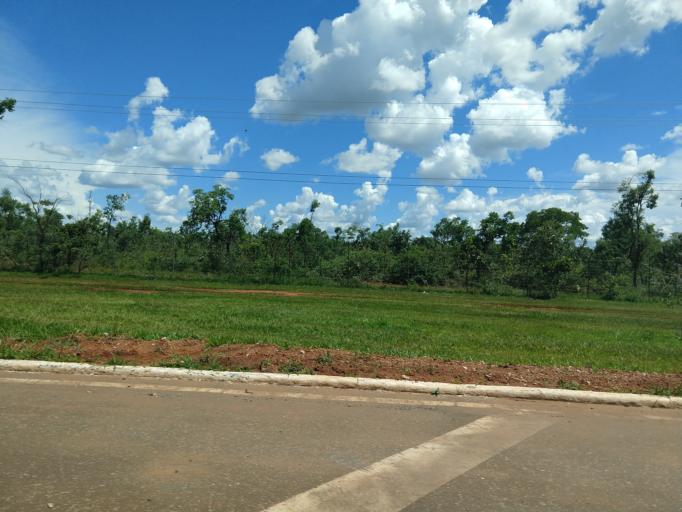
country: BR
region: Federal District
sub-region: Brasilia
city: Brasilia
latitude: -15.8019
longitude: -47.8488
